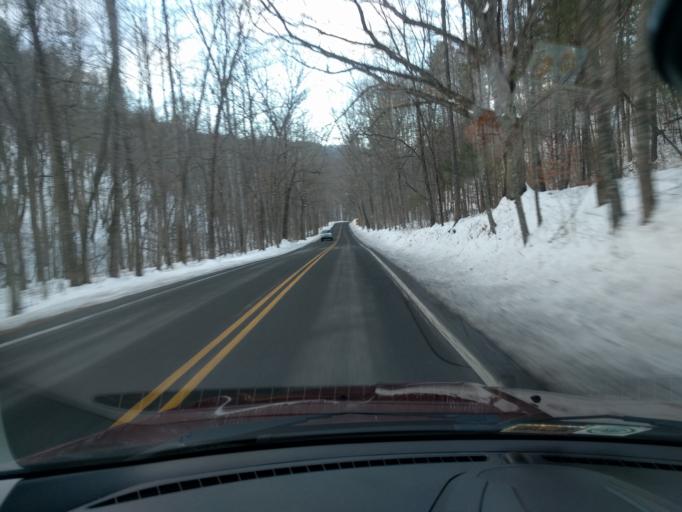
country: US
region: Virginia
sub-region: Bath County
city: Warm Springs
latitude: 38.0861
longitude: -79.8613
